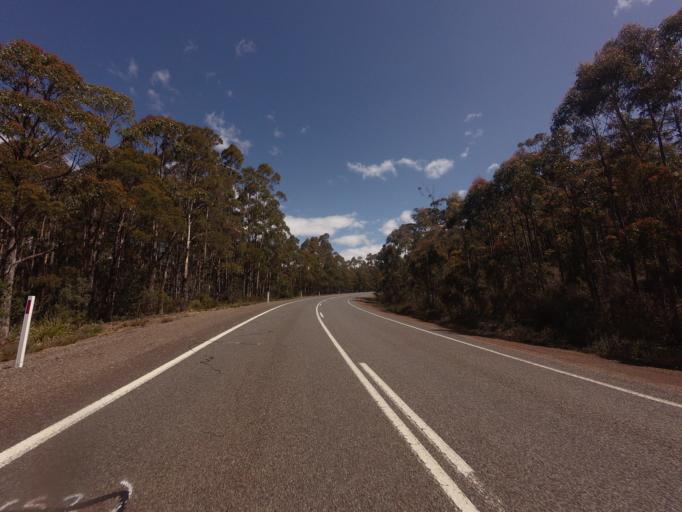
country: AU
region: Tasmania
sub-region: Northern Midlands
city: Evandale
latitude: -42.0121
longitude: 147.8726
